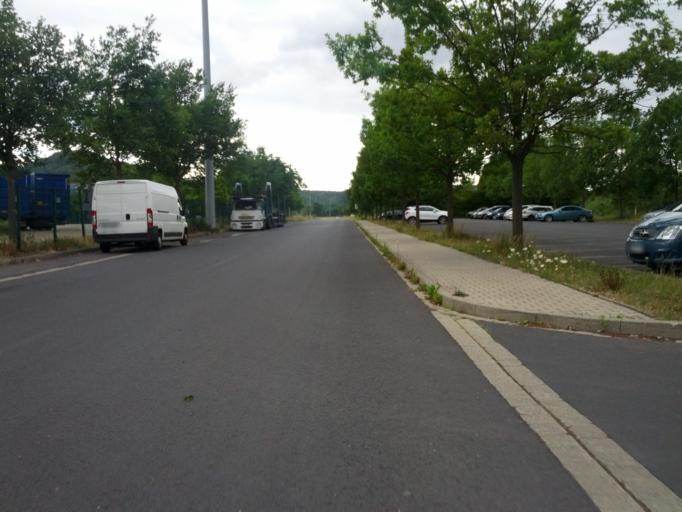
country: DE
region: Thuringia
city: Krauthausen
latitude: 50.9862
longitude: 10.2681
